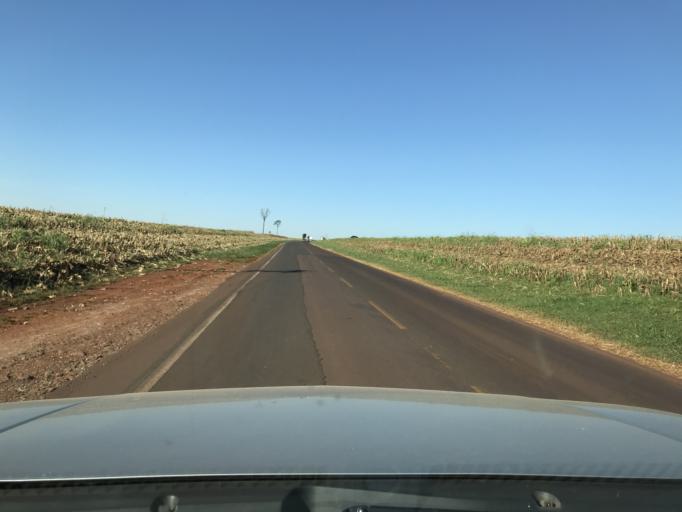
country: BR
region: Parana
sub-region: Palotina
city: Palotina
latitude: -24.2109
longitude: -53.8480
